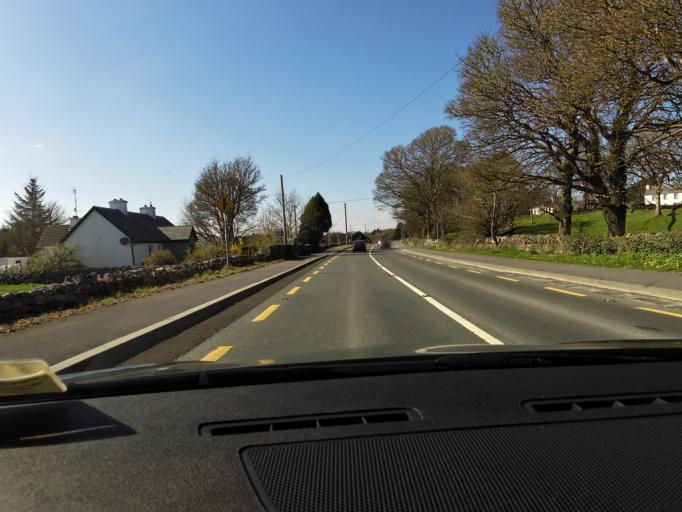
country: IE
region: Connaught
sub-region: County Galway
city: Oughterard
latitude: 53.3940
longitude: -9.2524
